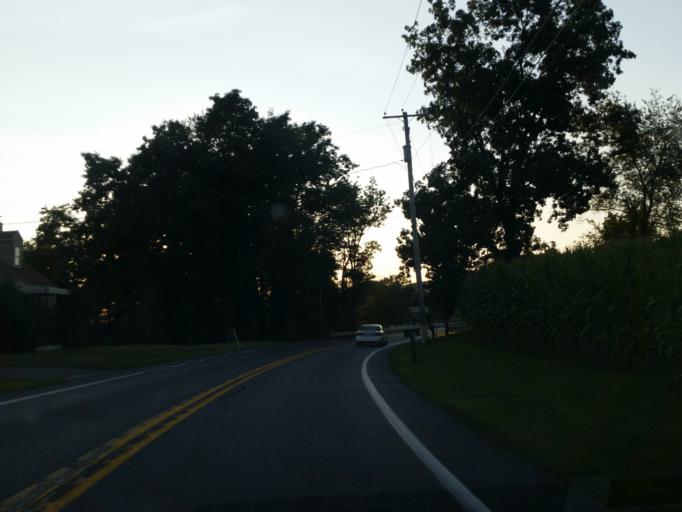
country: US
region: Pennsylvania
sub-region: Lancaster County
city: Reinholds
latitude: 40.2817
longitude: -76.1504
